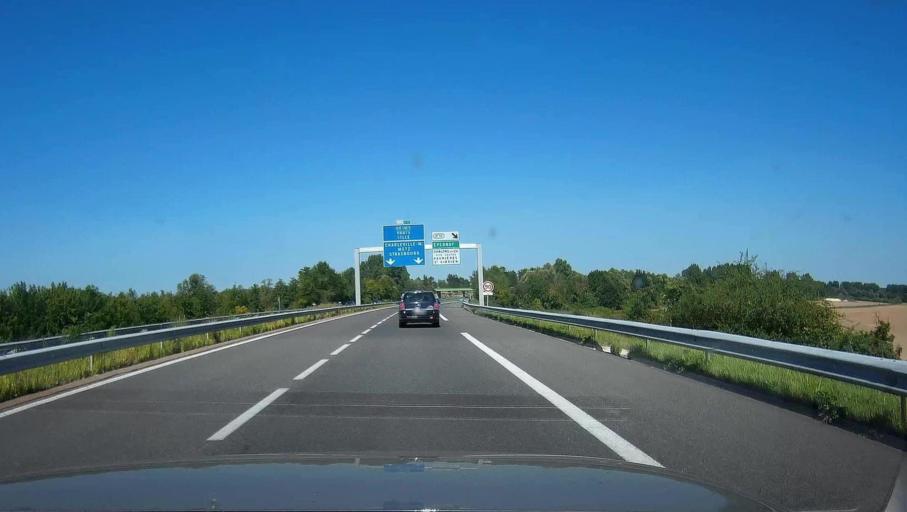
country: FR
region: Champagne-Ardenne
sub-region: Departement de la Marne
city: Fagnieres
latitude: 48.9663
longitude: 4.2843
